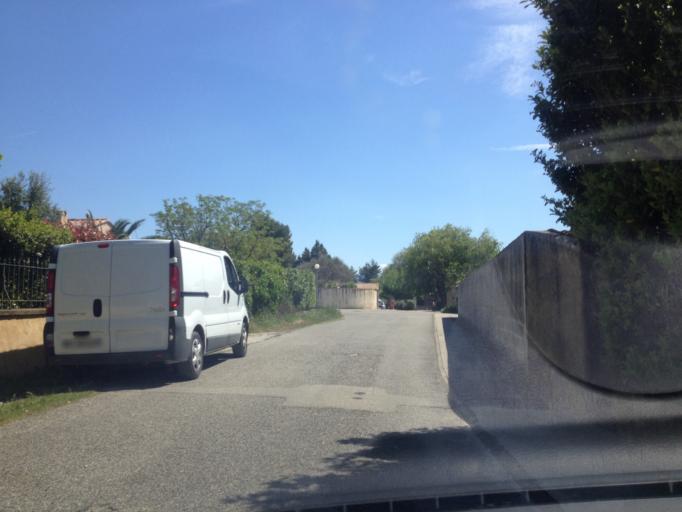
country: FR
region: Provence-Alpes-Cote d'Azur
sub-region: Departement du Vaucluse
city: Camaret-sur-Aigues
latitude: 44.1623
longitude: 4.8646
